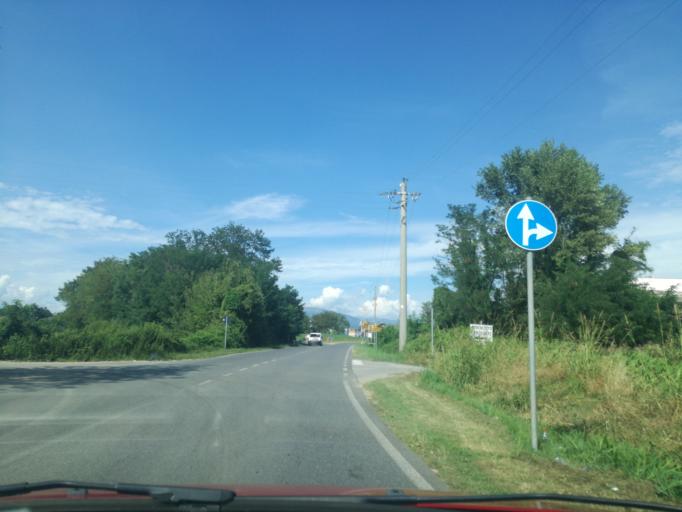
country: IT
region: Lombardy
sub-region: Provincia di Monza e Brianza
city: Busnago
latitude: 45.6233
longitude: 9.4660
